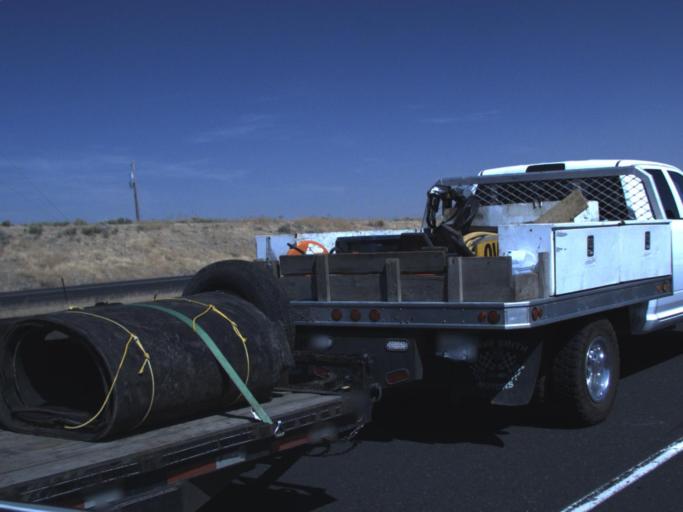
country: US
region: Washington
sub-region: Adams County
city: Ritzville
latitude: 47.0960
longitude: -118.6860
